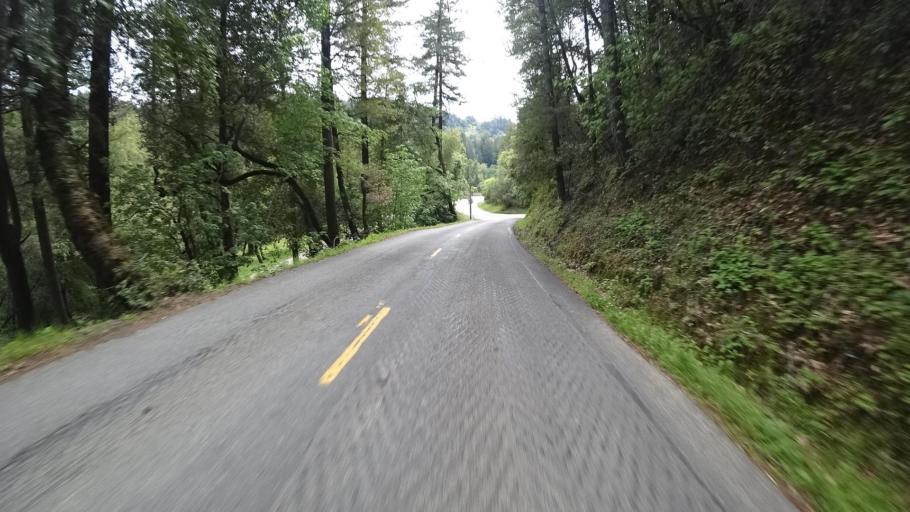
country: US
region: California
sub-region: Humboldt County
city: Redway
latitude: 40.0927
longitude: -123.8010
